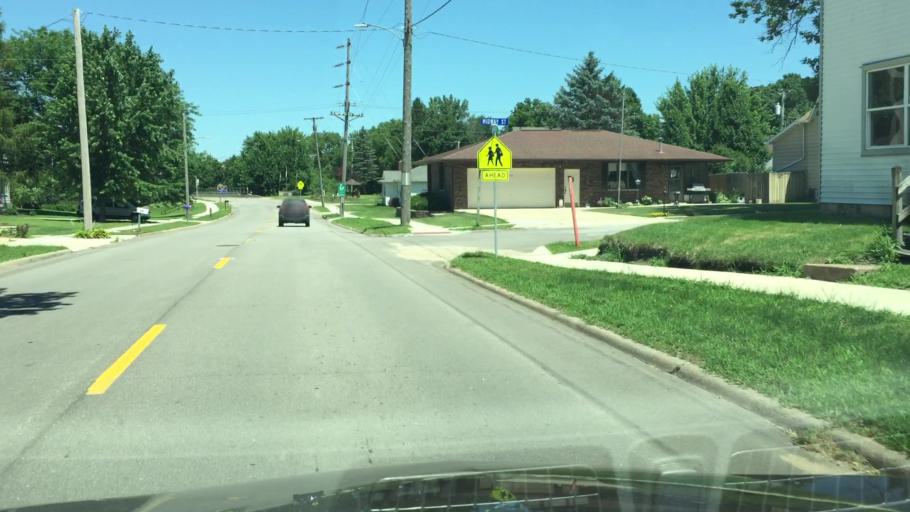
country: US
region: Iowa
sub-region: Cedar County
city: Mechanicsville
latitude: 41.9940
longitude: -91.1415
